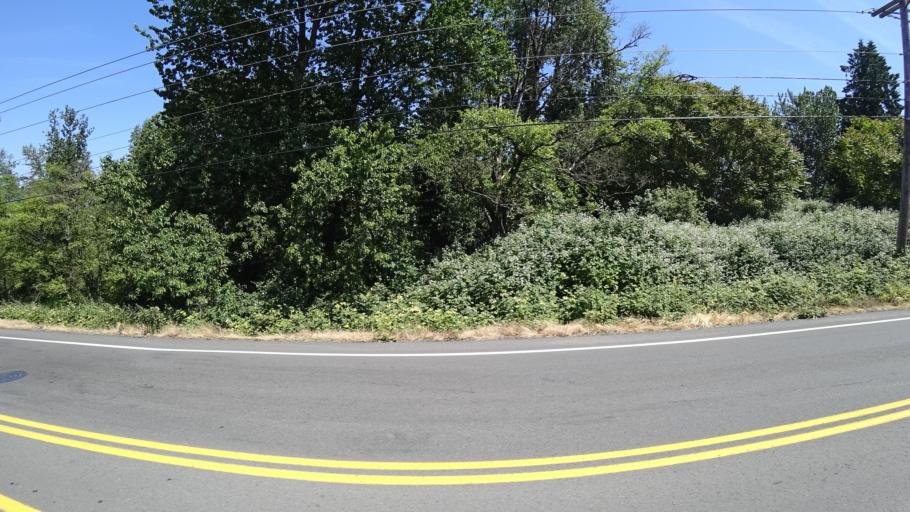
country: US
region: Oregon
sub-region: Multnomah County
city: Fairview
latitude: 45.5432
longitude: -122.4334
